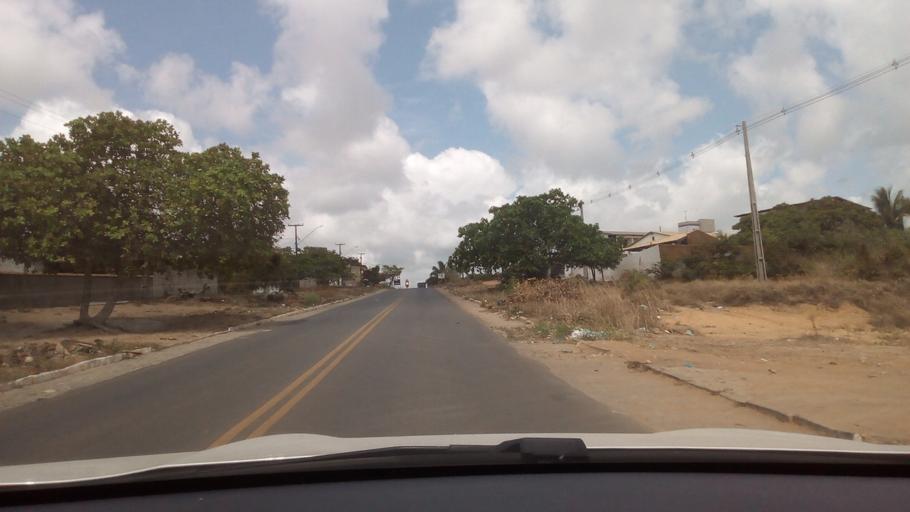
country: BR
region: Paraiba
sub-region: Conde
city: Conde
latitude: -7.2765
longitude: -34.8043
